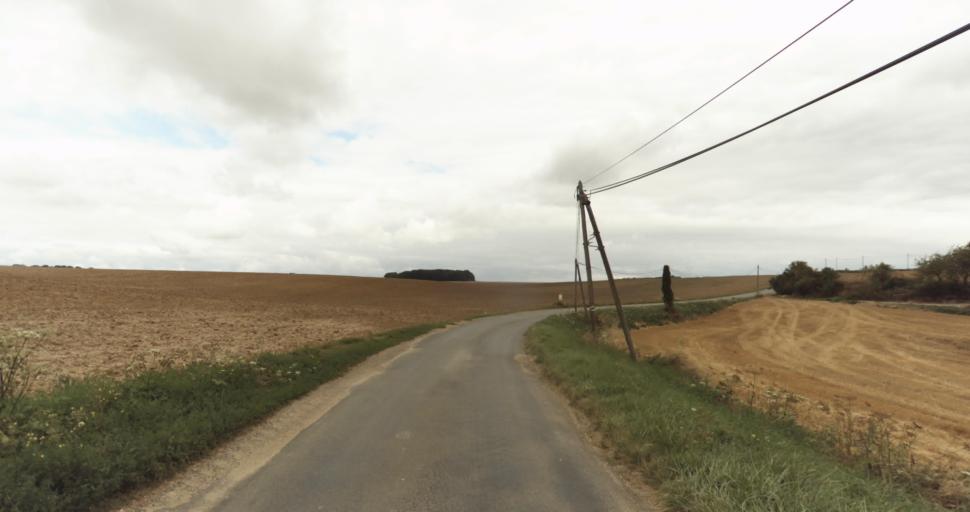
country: FR
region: Haute-Normandie
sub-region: Departement de l'Eure
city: Menilles
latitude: 49.0196
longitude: 1.3020
